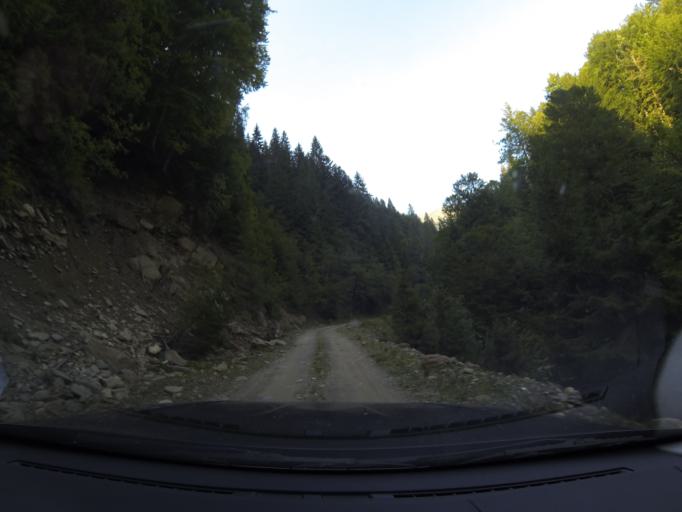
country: RO
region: Arges
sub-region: Comuna Arefu
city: Arefu
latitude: 45.5137
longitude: 24.6755
